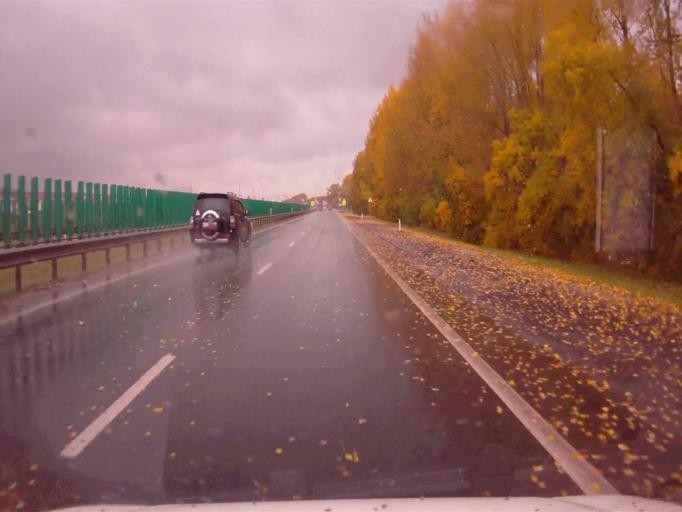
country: RU
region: Chelyabinsk
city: Dolgoderevenskoye
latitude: 55.2802
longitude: 61.3433
